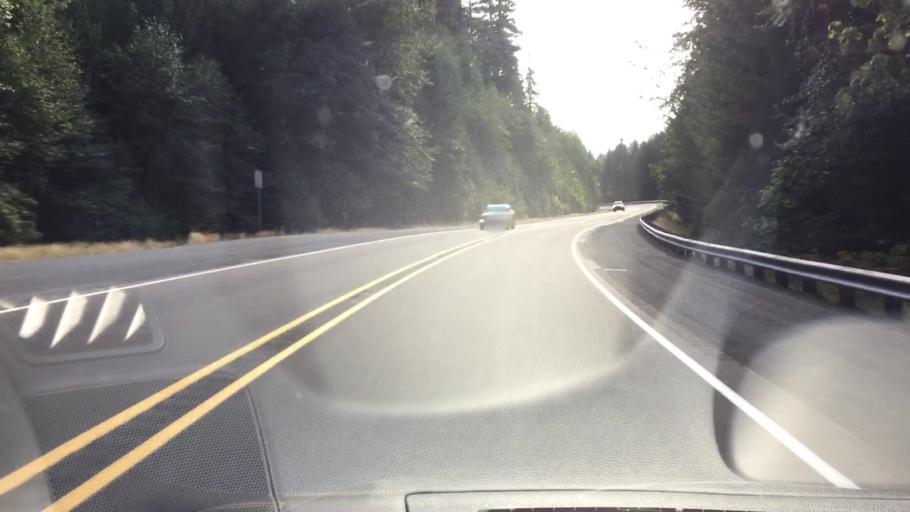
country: US
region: Washington
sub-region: Pierce County
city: Buckley
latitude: 46.6738
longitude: -121.5790
